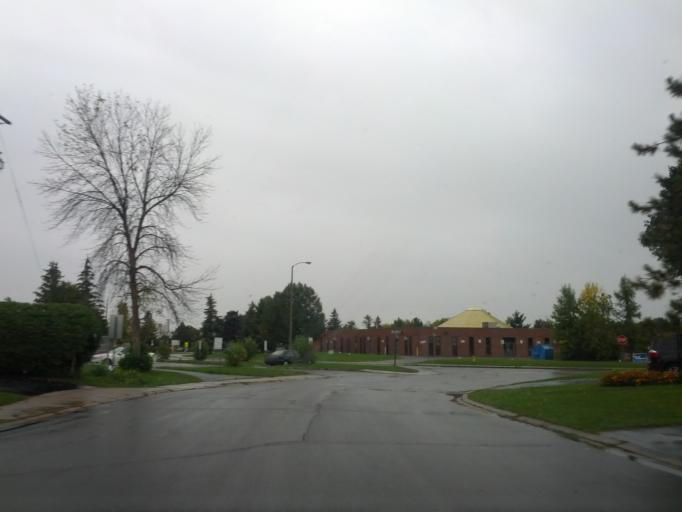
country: CA
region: Quebec
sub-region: Outaouais
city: Gatineau
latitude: 45.4732
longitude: -75.5098
